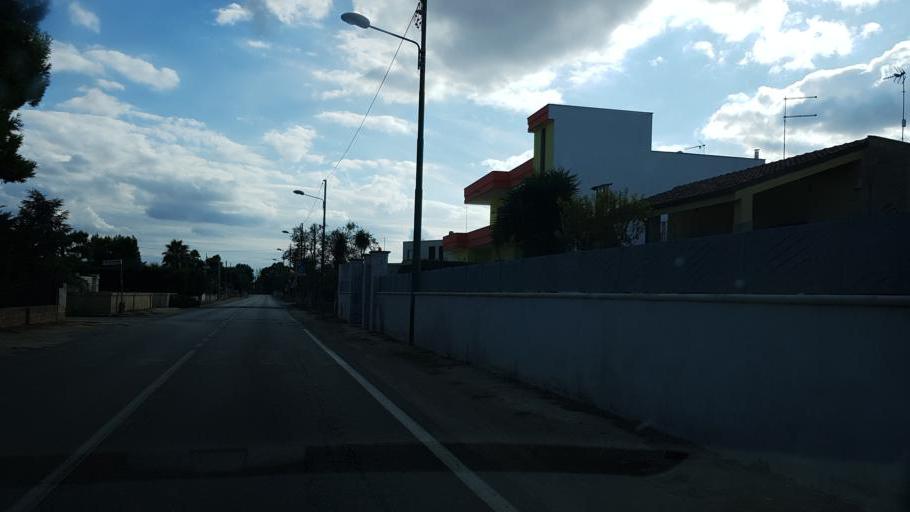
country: IT
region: Apulia
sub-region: Provincia di Lecce
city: Nardo
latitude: 40.1541
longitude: 18.0187
